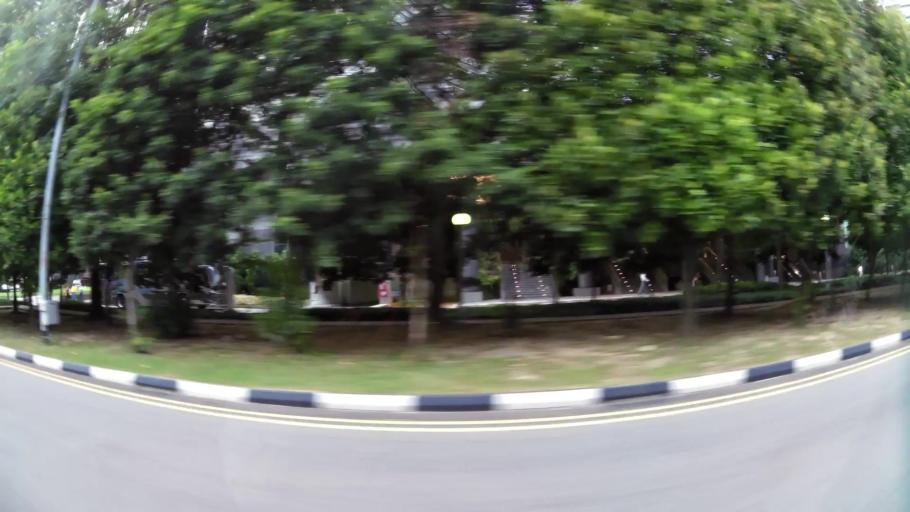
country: SG
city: Singapore
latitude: 1.2994
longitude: 103.8613
